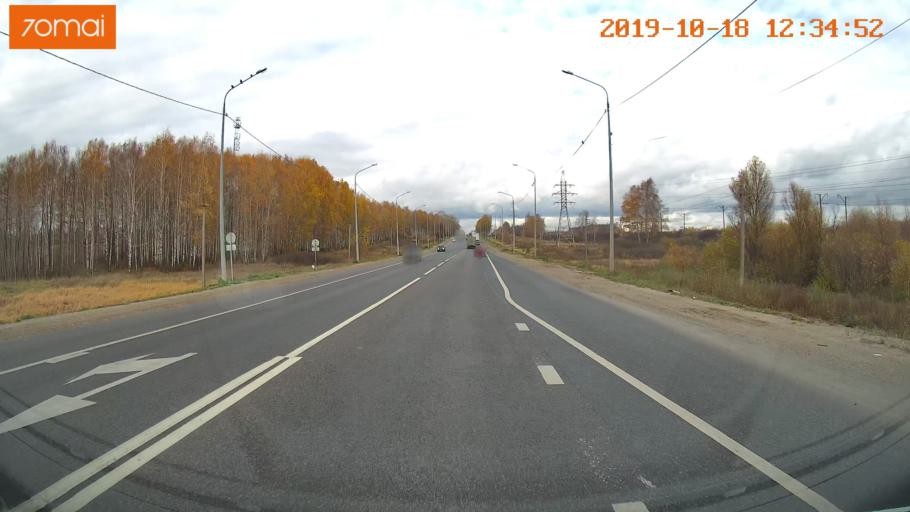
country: RU
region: Rjazan
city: Ryazan'
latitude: 54.6185
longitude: 39.6366
